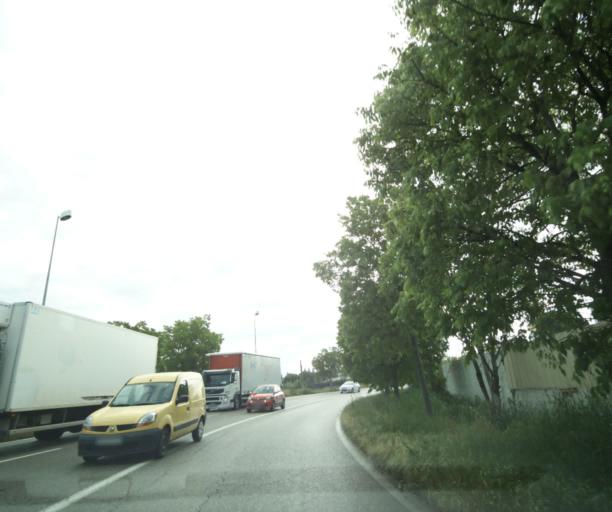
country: FR
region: Provence-Alpes-Cote d'Azur
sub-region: Departement des Bouches-du-Rhone
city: Cabries
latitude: 43.4943
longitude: 5.3696
